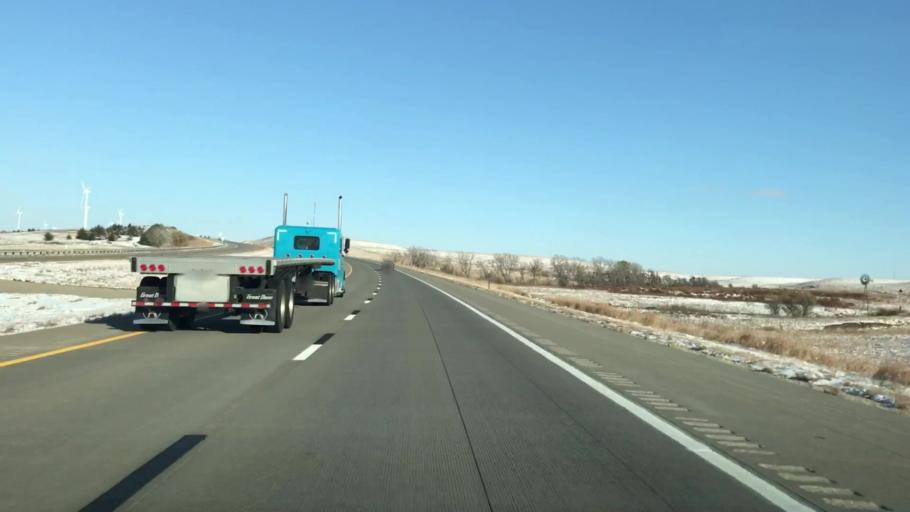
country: US
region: Kansas
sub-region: Lincoln County
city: Lincoln
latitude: 38.8679
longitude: -98.0695
